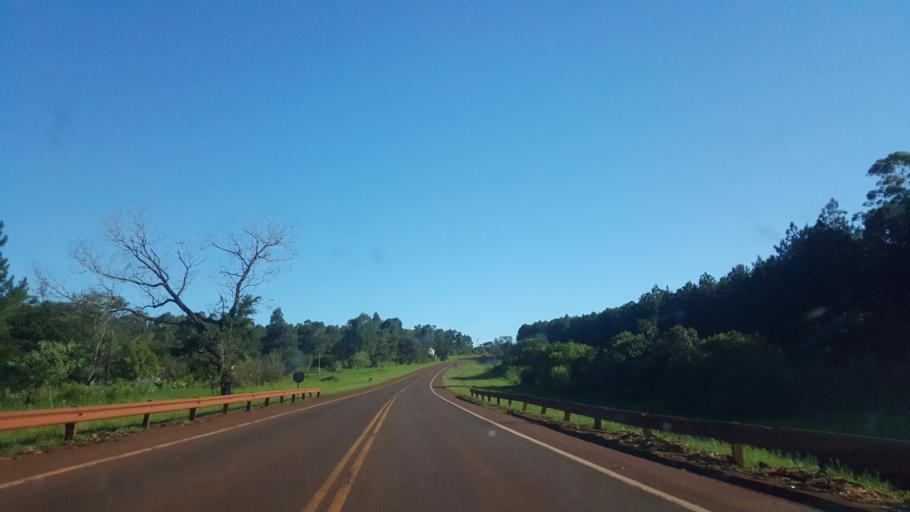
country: AR
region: Misiones
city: Puerto Esperanza
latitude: -26.1646
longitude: -54.5837
